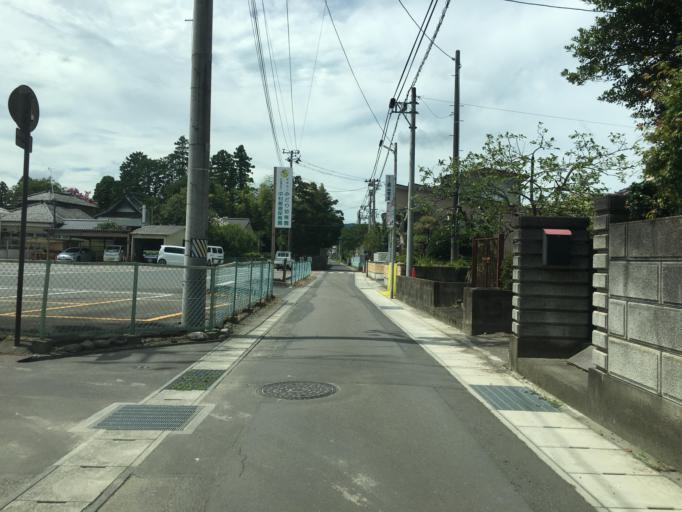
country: JP
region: Miyagi
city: Marumori
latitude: 37.7953
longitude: 140.9187
